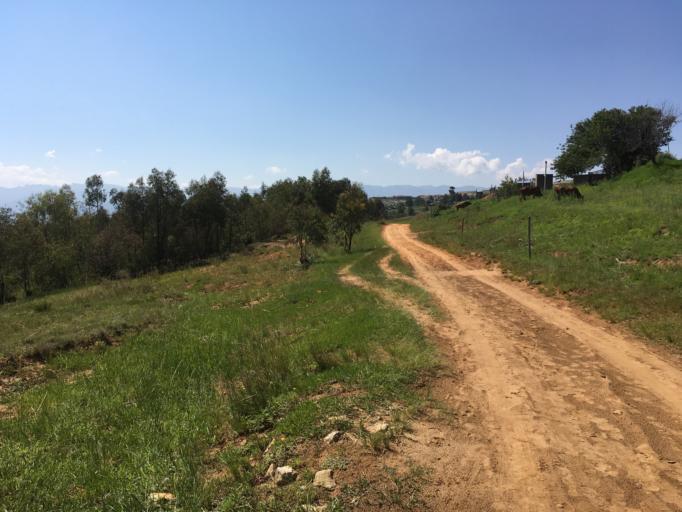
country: LS
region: Butha-Buthe
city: Butha-Buthe
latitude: -28.7228
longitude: 28.3596
